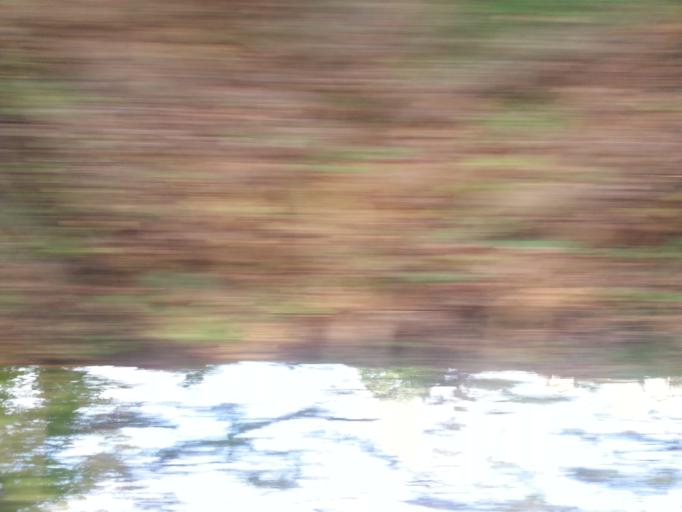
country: US
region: Tennessee
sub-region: Blount County
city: Wildwood
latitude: 35.8439
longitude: -83.8713
